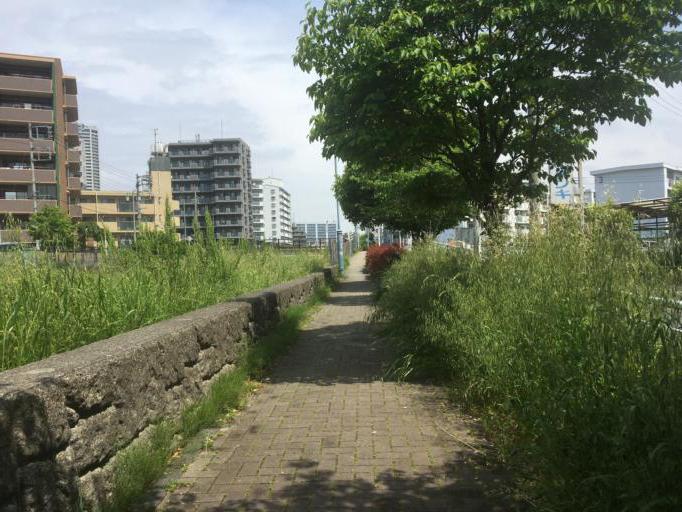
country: JP
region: Saitama
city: Shimotoda
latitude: 35.8410
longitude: 139.6514
